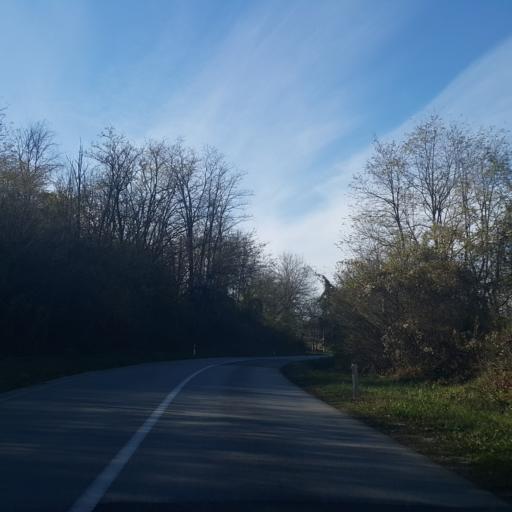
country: RS
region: Central Serbia
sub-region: Sumadijski Okrug
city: Topola
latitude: 44.2478
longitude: 20.7050
